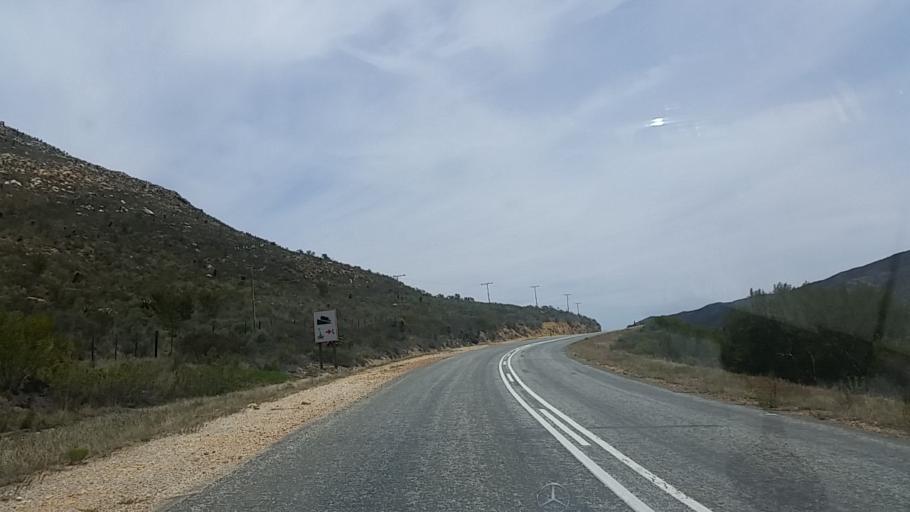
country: ZA
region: Western Cape
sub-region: Eden District Municipality
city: Knysna
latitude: -33.7466
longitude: 22.9852
